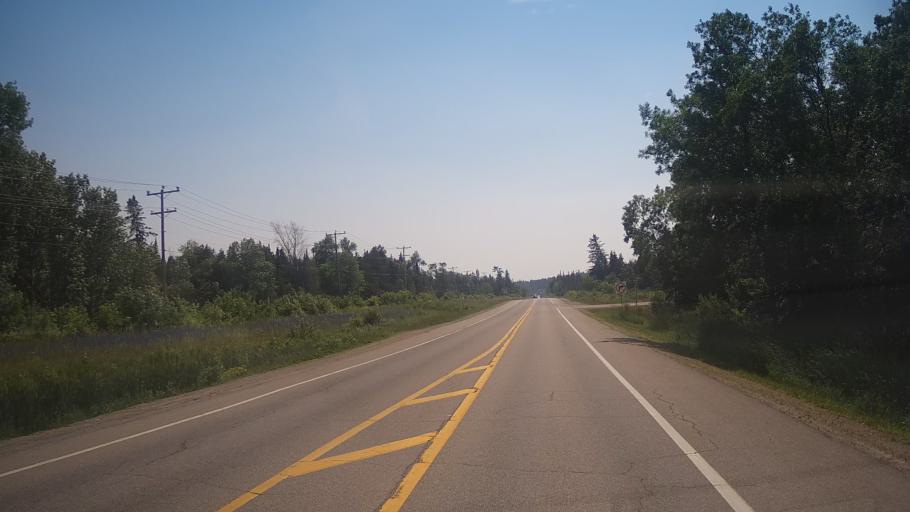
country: CA
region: Ontario
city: Pembroke
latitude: 45.8245
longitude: -77.0179
